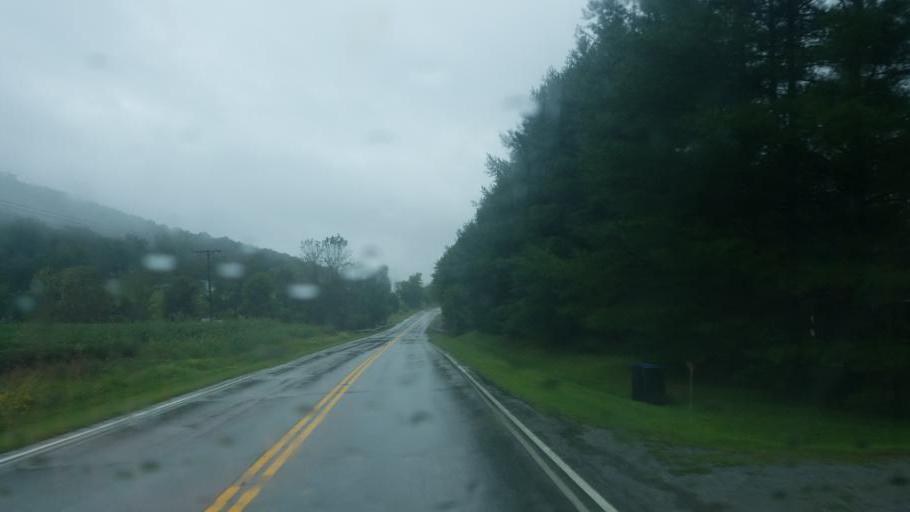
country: US
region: Kentucky
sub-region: Fleming County
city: Flemingsburg
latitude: 38.3333
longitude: -83.5929
